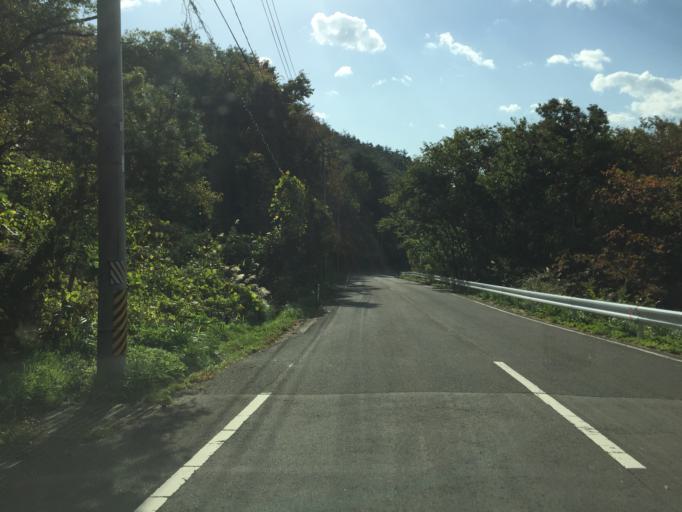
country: JP
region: Fukushima
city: Fukushima-shi
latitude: 37.8068
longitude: 140.3888
